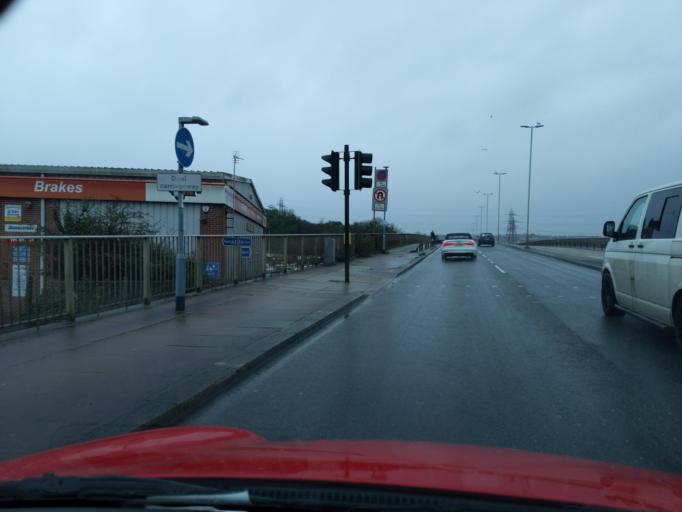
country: GB
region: England
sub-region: Plymouth
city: Plymstock
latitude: 50.3680
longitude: -4.1072
